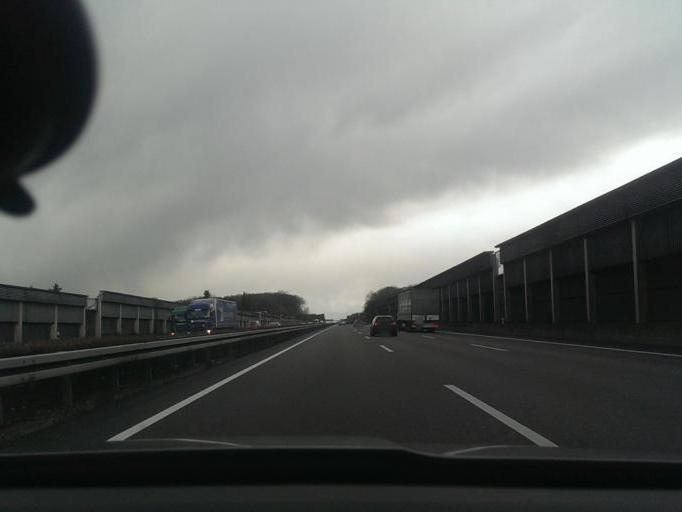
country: DE
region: Lower Saxony
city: Lehre
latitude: 52.3109
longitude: 10.5967
